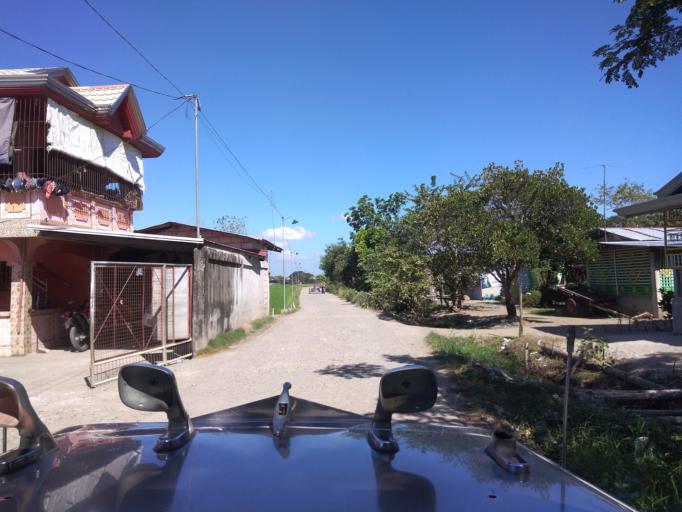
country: PH
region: Central Luzon
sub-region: Province of Pampanga
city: Batasan Bata
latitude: 15.1606
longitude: 120.9192
